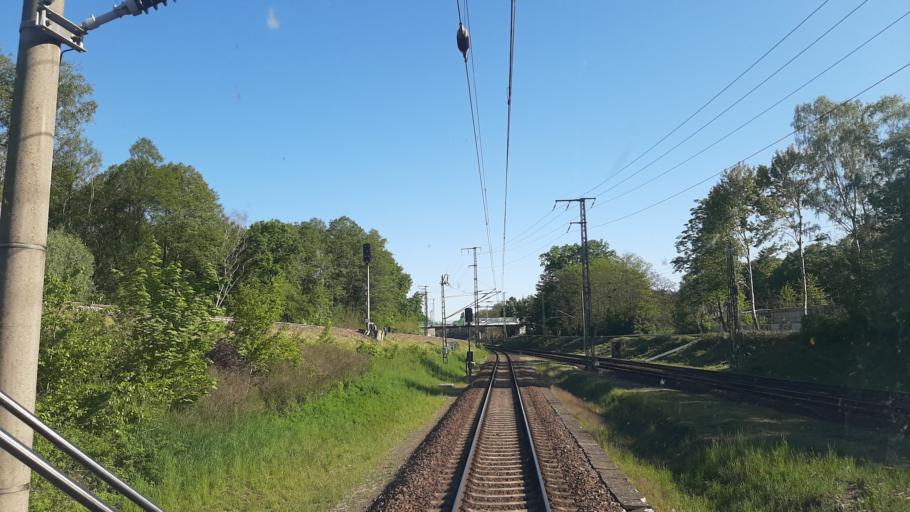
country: DE
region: Brandenburg
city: Birkenwerder
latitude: 52.6806
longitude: 13.2882
